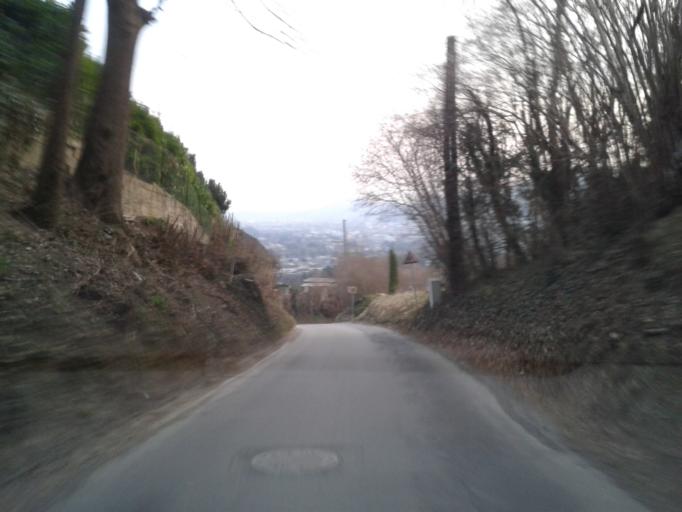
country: AT
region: Styria
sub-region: Politischer Bezirk Graz-Umgebung
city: Stattegg
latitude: 47.1257
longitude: 15.4370
